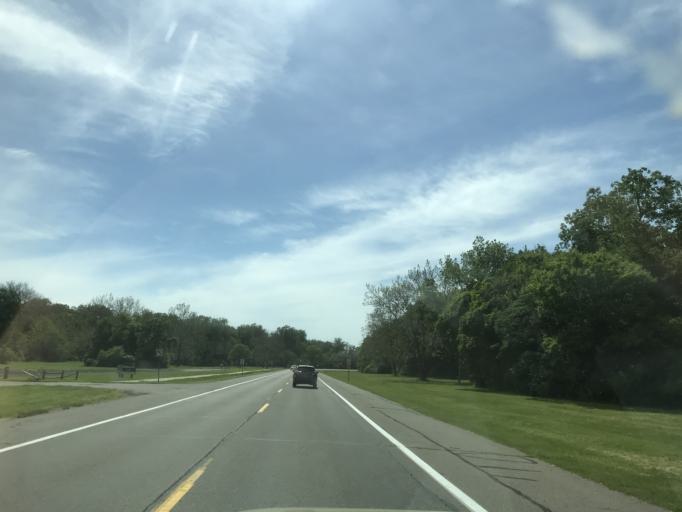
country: US
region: Michigan
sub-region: Wayne County
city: Dearborn Heights
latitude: 42.3476
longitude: -83.2830
